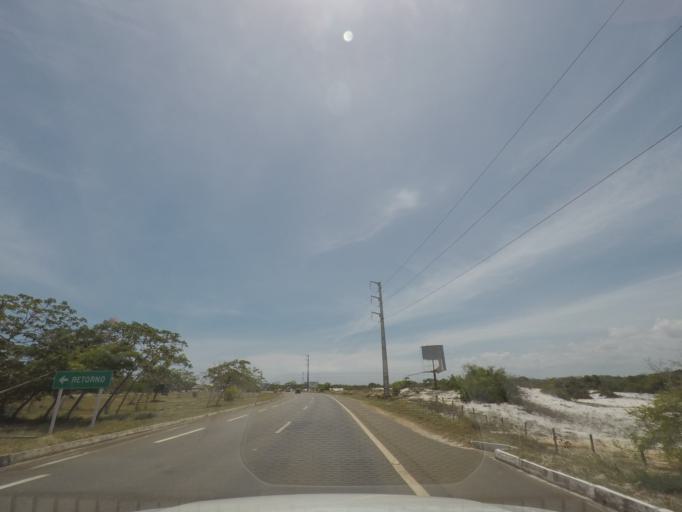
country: BR
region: Bahia
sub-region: Mata De Sao Joao
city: Mata de Sao Joao
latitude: -12.6387
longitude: -38.0712
